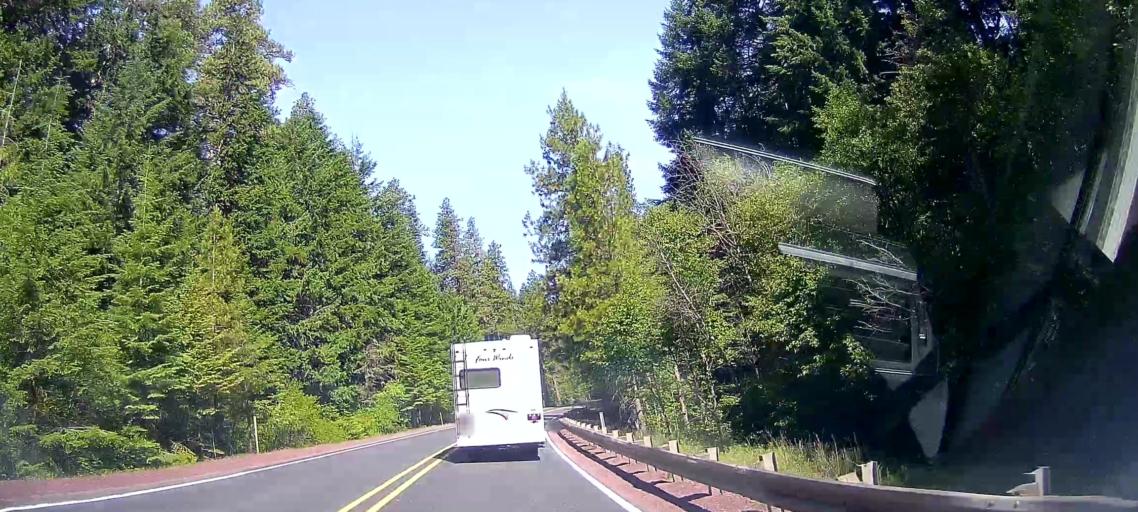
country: US
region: Oregon
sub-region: Jefferson County
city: Warm Springs
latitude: 45.0738
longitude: -121.5348
